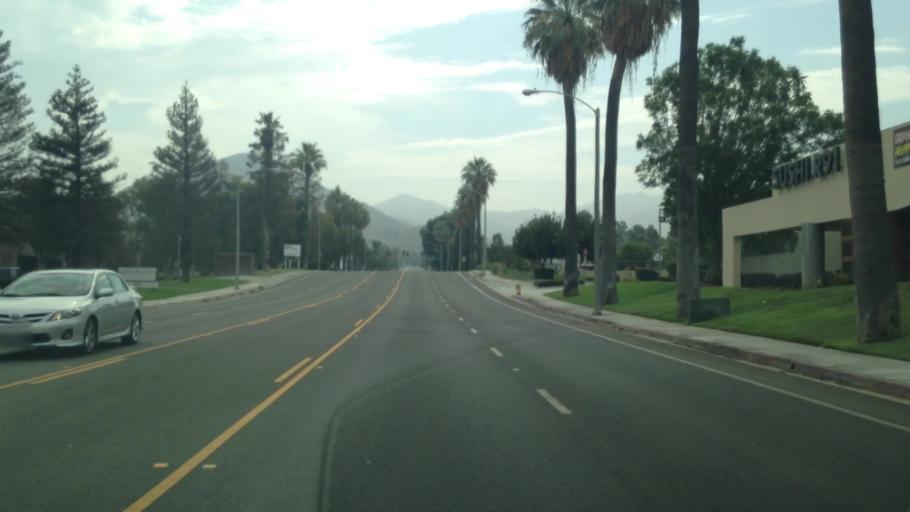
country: US
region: California
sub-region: Riverside County
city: Highgrove
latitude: 33.9903
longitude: -117.3473
